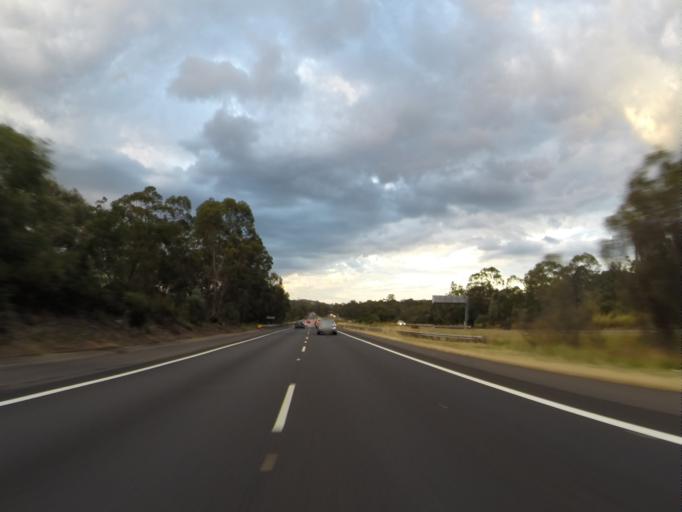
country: AU
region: New South Wales
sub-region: Wollondilly
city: Douglas Park
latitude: -34.1936
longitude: 150.7108
